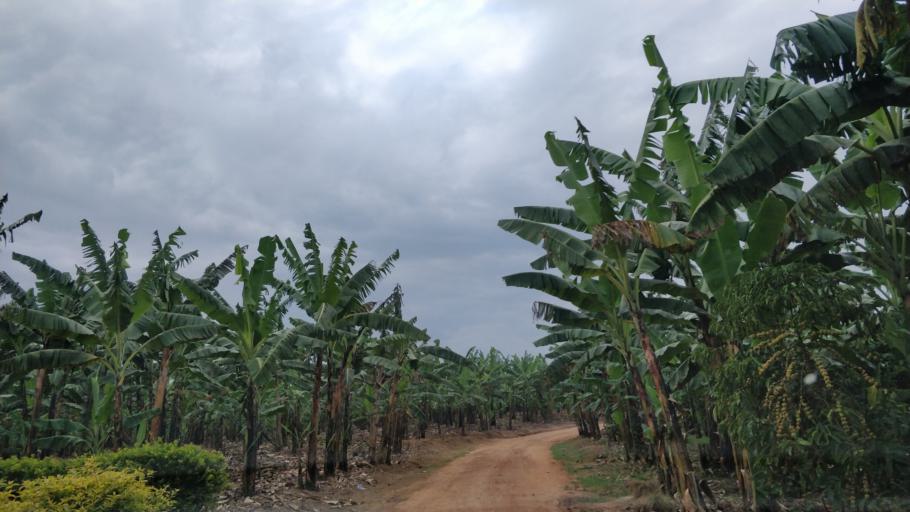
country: UG
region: Western Region
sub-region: Sheema District
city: Kibingo
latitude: -0.6407
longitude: 30.4902
